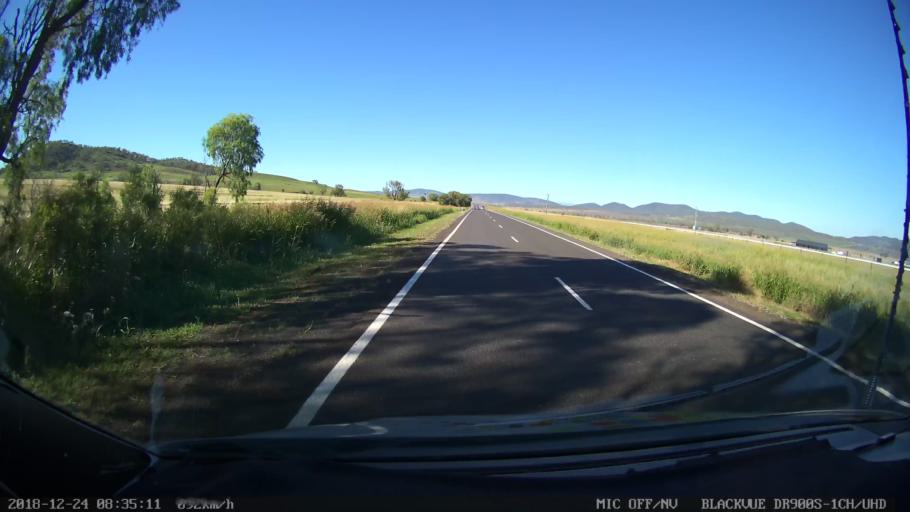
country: AU
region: New South Wales
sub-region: Liverpool Plains
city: Quirindi
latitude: -31.2995
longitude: 150.6613
